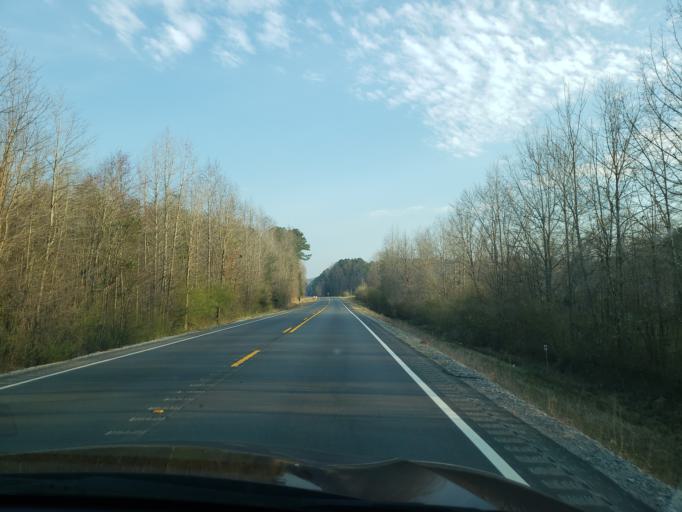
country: US
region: Alabama
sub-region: Hale County
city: Greensboro
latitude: 32.8263
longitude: -87.6030
